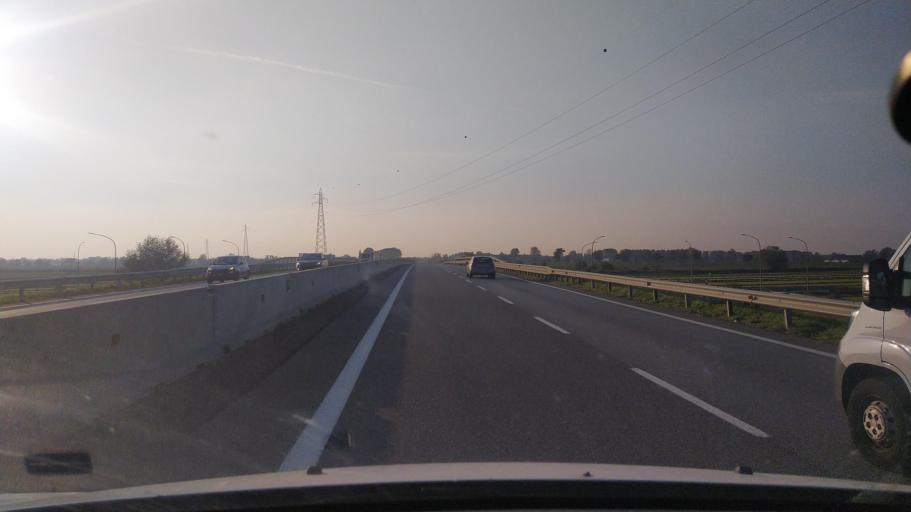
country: IT
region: Lombardy
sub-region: Provincia di Cremona
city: Nosadello
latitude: 45.3891
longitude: 9.5259
